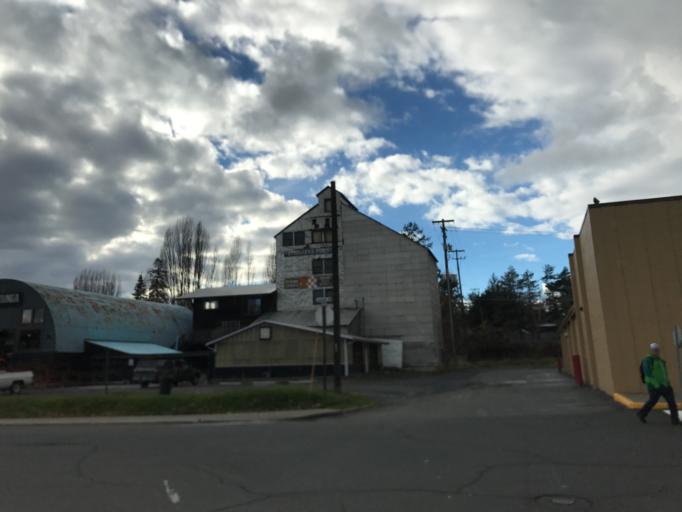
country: US
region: Idaho
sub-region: Latah County
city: Moscow
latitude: 46.7375
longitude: -117.0027
